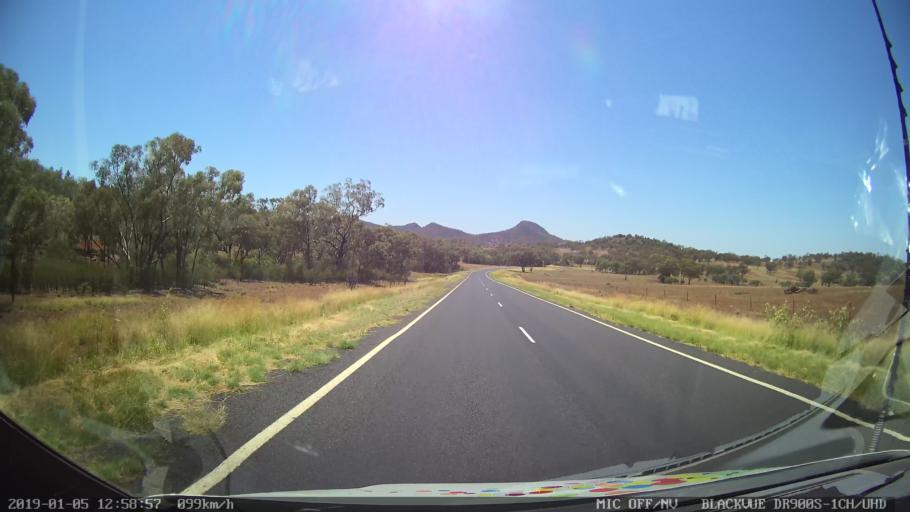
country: AU
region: New South Wales
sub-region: Narrabri
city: Boggabri
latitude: -31.1128
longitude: 149.7580
